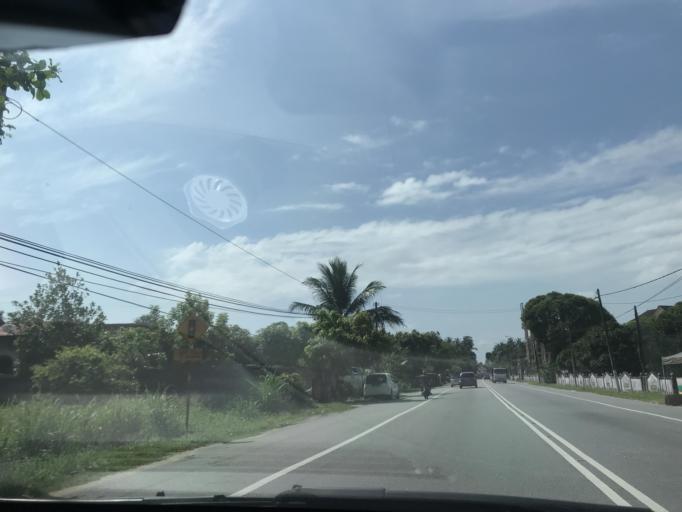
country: MY
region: Kelantan
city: Tumpat
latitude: 6.1381
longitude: 102.1709
